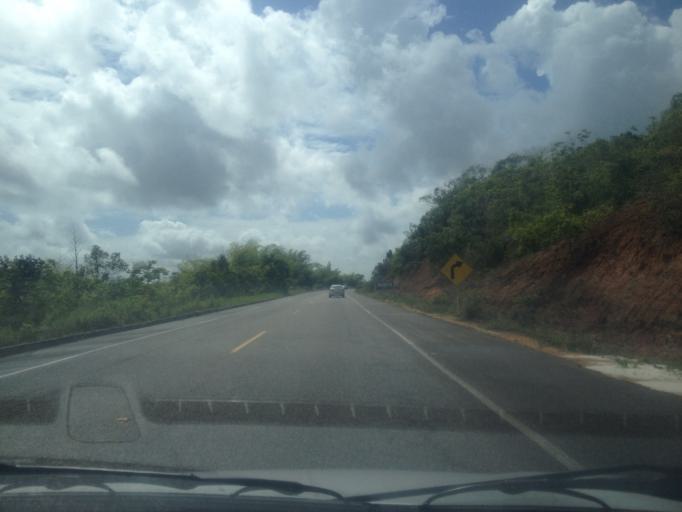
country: BR
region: Bahia
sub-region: Conde
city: Conde
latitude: -12.0695
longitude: -37.7484
